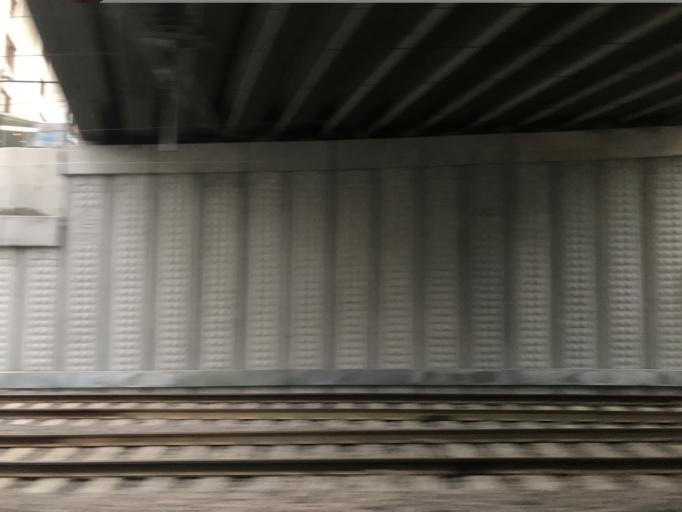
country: TR
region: Istanbul
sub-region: Atasehir
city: Atasehir
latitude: 40.9734
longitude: 29.0753
